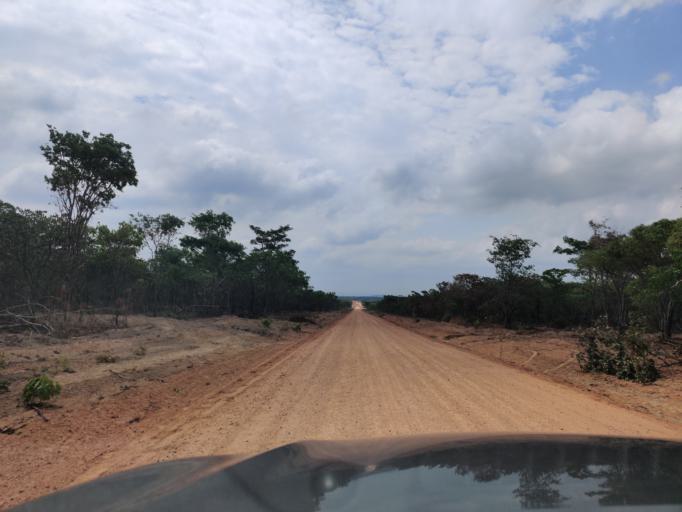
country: ZM
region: Central
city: Mkushi
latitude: -13.6755
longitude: 29.7527
